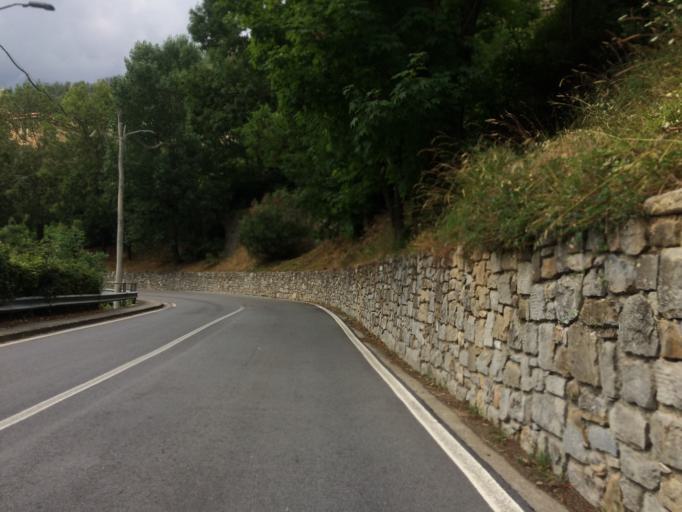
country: IT
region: Liguria
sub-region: Provincia di Imperia
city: Pigna
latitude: 43.9323
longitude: 7.6611
